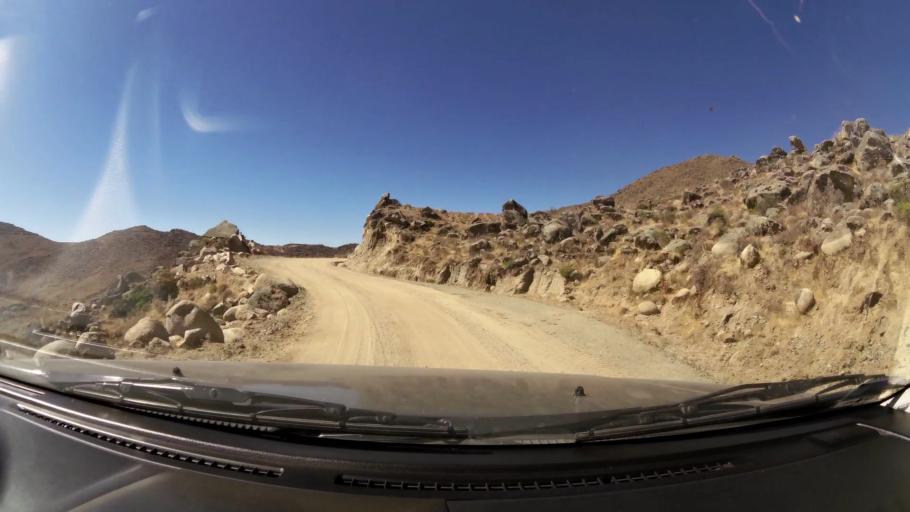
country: PE
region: Huancavelica
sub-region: Huaytara
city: Quito-Arma
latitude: -13.6341
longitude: -75.3634
